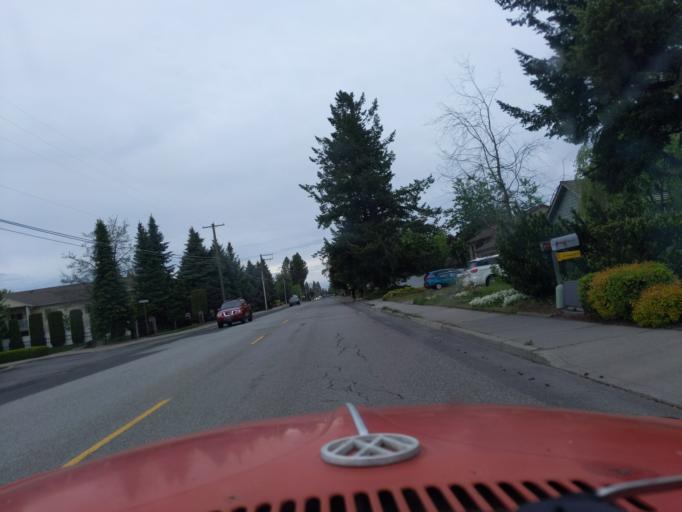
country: US
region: Washington
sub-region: Spokane County
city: Spokane
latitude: 47.5979
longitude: -117.3686
